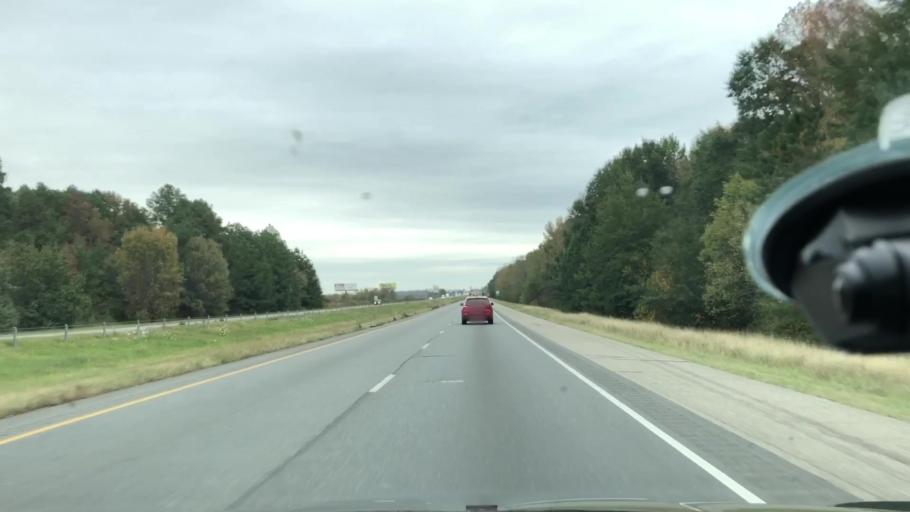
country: US
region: Arkansas
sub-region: Miller County
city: Texarkana
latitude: 33.4891
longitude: -93.9716
